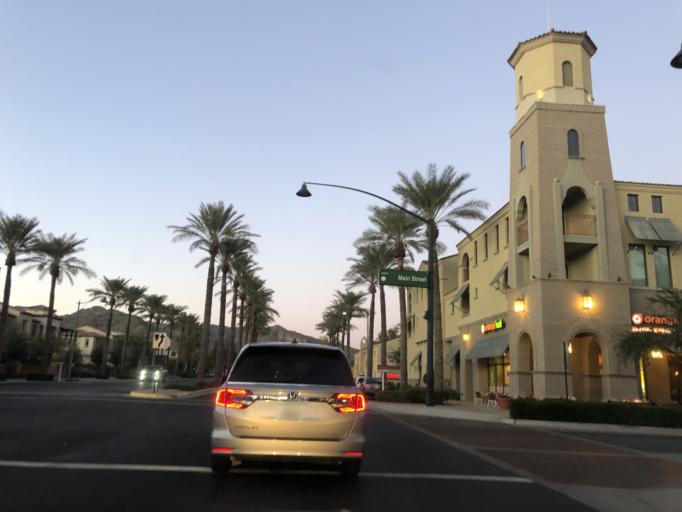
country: US
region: Arizona
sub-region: Maricopa County
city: Citrus Park
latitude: 33.4957
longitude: -112.5134
